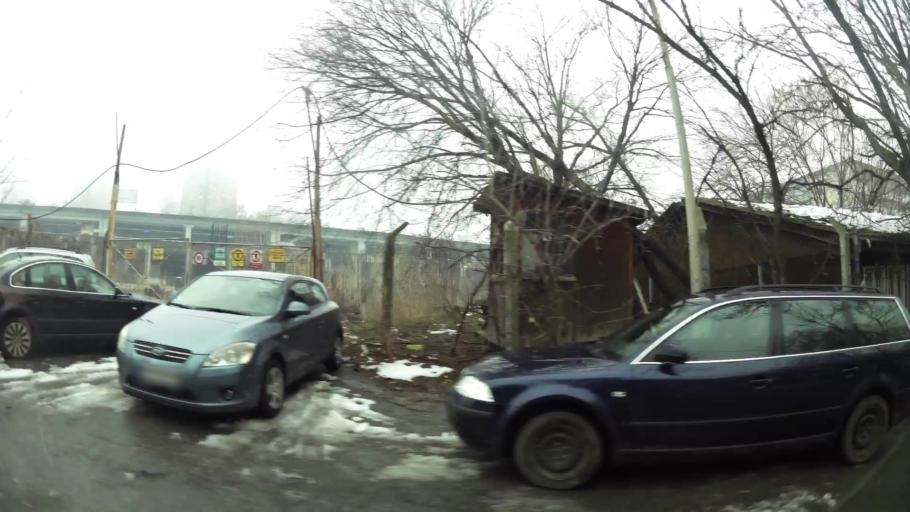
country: RS
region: Central Serbia
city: Belgrade
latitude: 44.7948
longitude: 20.4540
